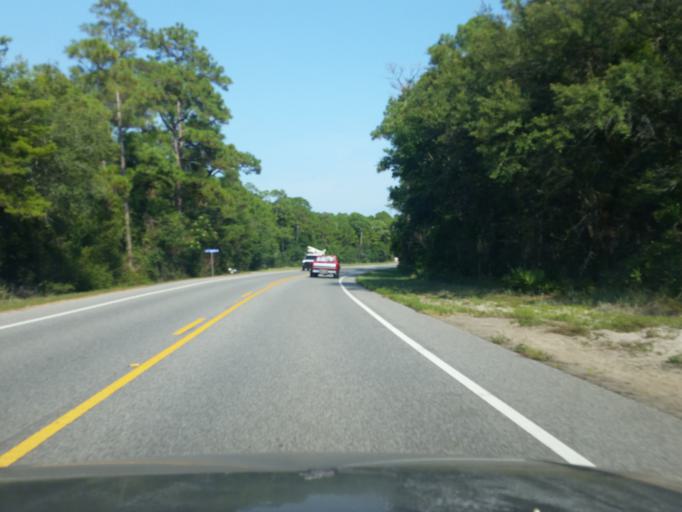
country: US
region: Alabama
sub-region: Baldwin County
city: Gulf Shores
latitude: 30.2481
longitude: -87.7916
